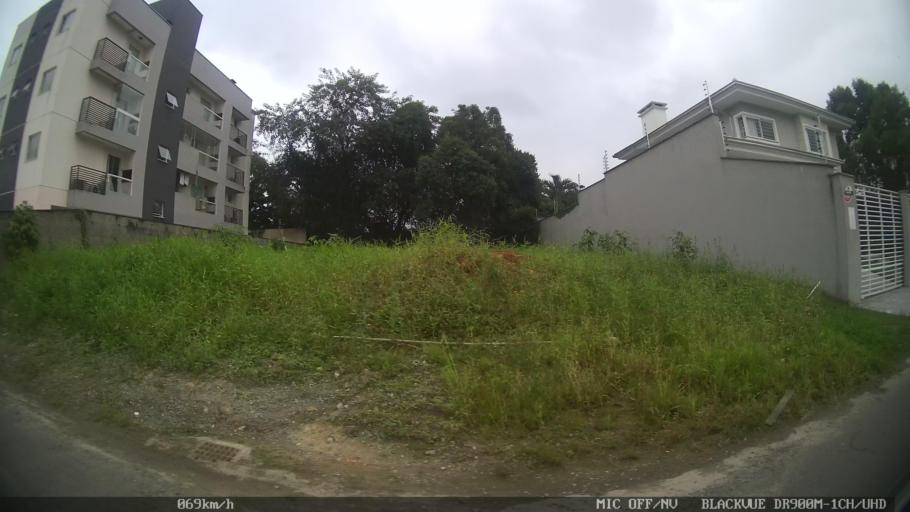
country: BR
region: Santa Catarina
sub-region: Joinville
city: Joinville
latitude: -26.2728
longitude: -48.8665
